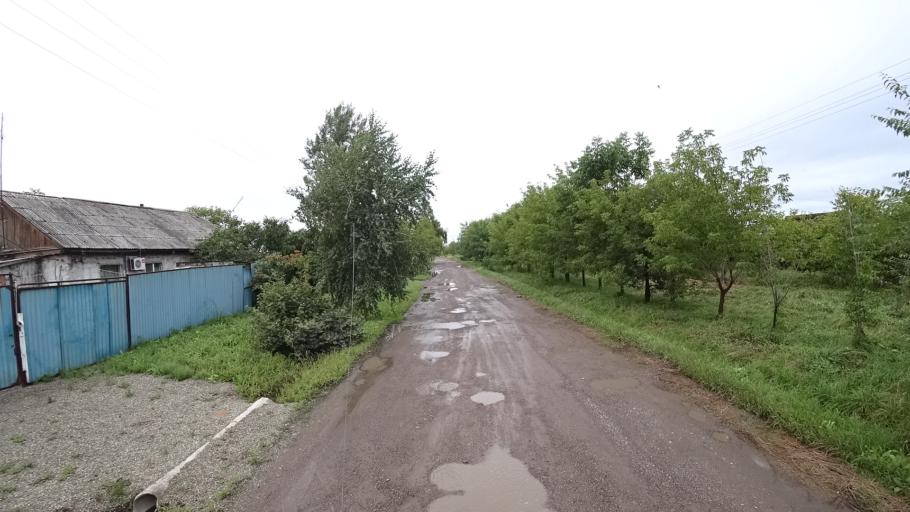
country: RU
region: Primorskiy
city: Monastyrishche
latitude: 44.1961
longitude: 132.4715
